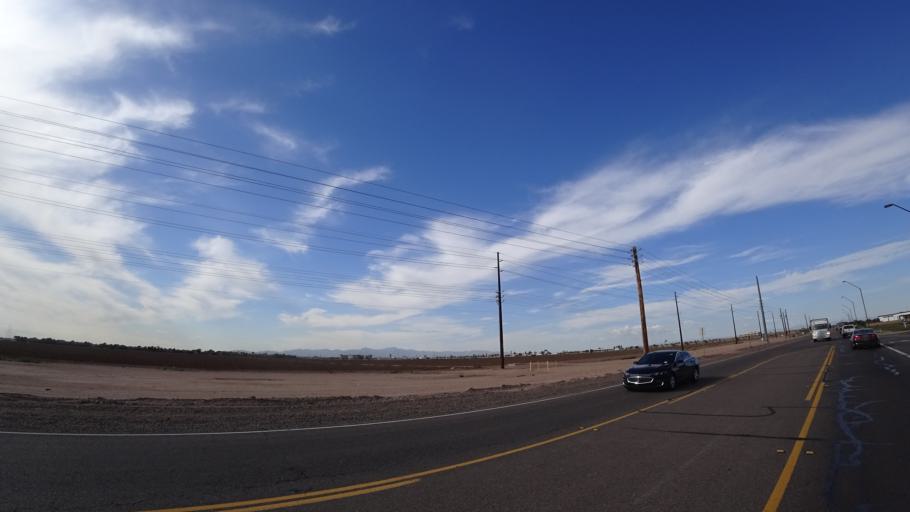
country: US
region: Arizona
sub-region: Maricopa County
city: Tolleson
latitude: 33.4527
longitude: -112.2899
